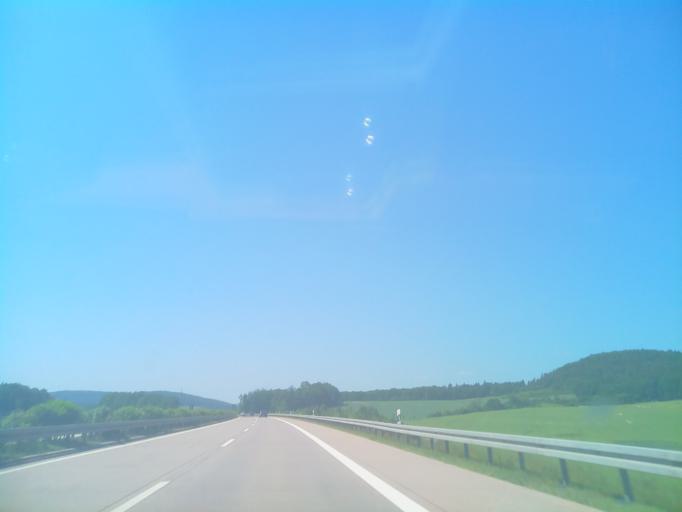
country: DE
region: Thuringia
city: Wolfershausen
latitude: 50.4761
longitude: 10.4508
